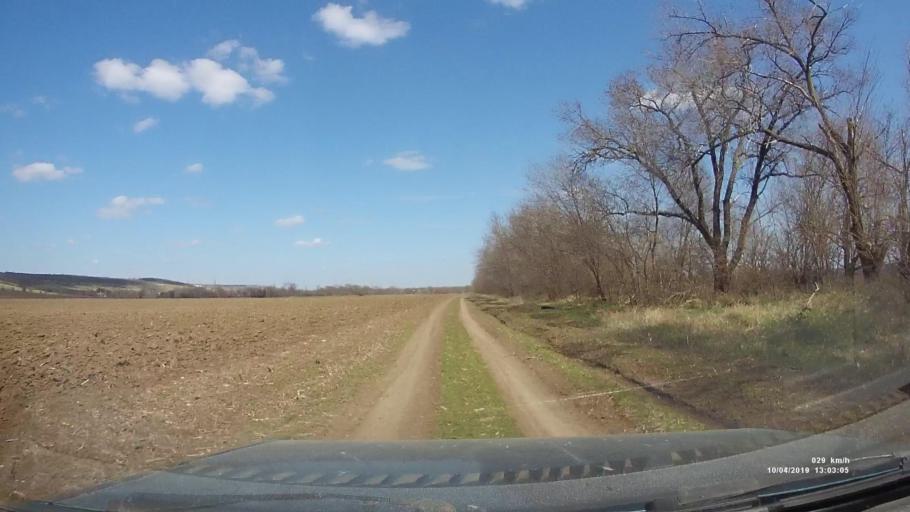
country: RU
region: Rostov
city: Masalovka
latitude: 48.3834
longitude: 40.2337
